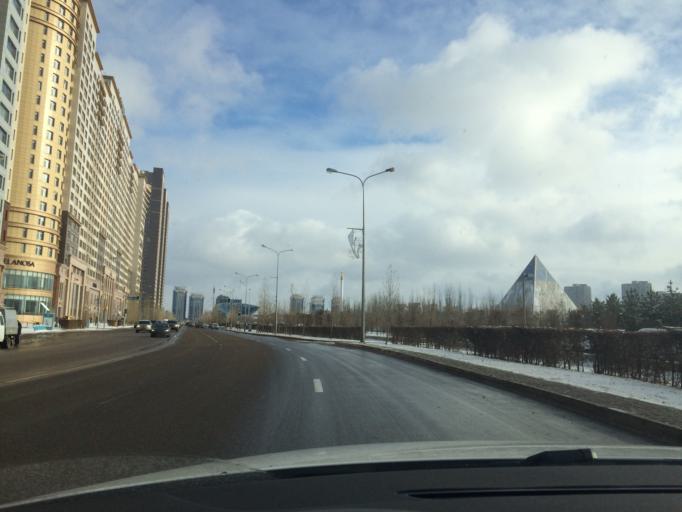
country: KZ
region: Astana Qalasy
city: Astana
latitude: 51.1275
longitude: 71.4588
